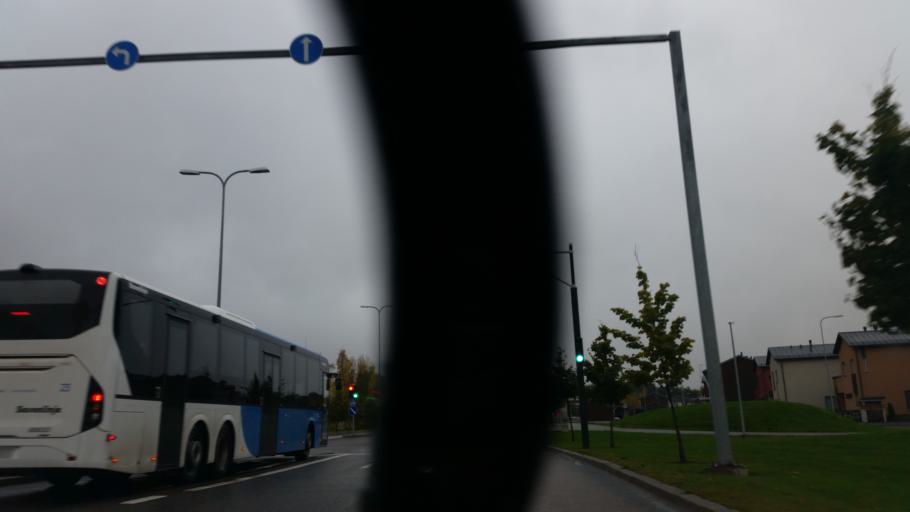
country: FI
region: Uusimaa
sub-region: Helsinki
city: Vantaa
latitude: 60.2827
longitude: 25.0122
